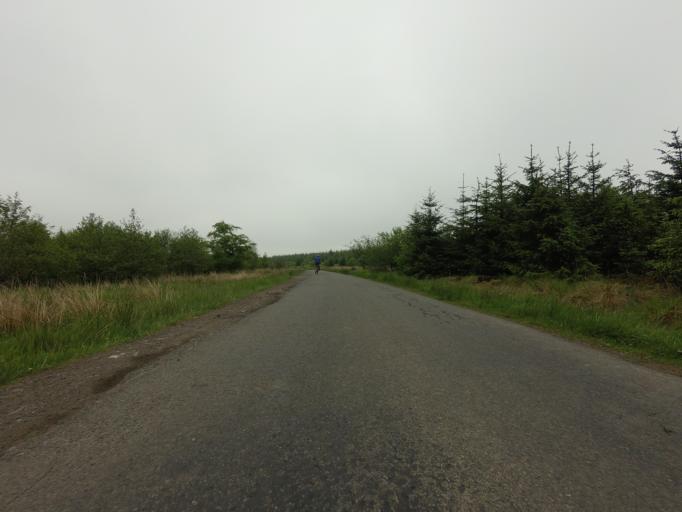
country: GB
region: Scotland
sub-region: Fife
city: Townhill
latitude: 56.1295
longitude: -3.4419
